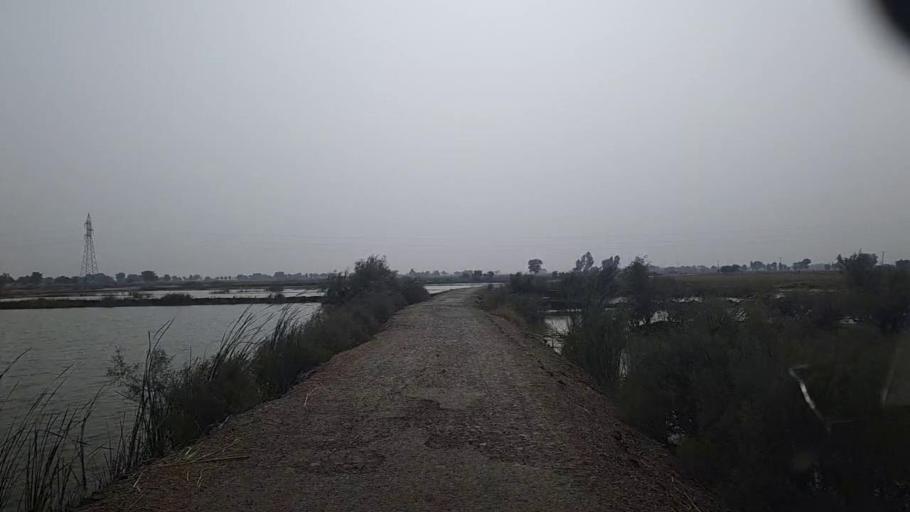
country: PK
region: Sindh
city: Kashmor
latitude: 28.3950
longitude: 69.4213
